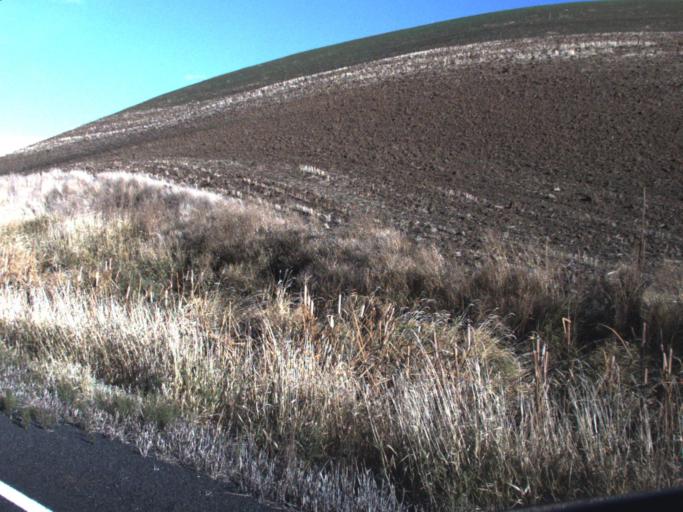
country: US
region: Washington
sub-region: Whitman County
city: Colfax
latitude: 46.7604
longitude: -117.3822
